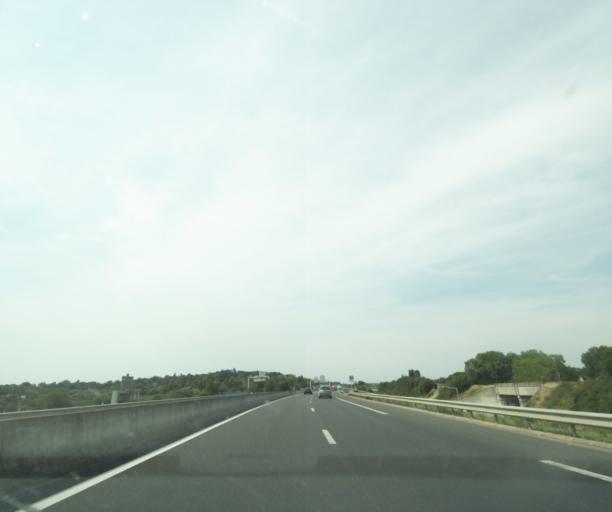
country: FR
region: Centre
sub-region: Departement d'Indre-et-Loire
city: La Riche
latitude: 47.3867
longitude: 0.6498
